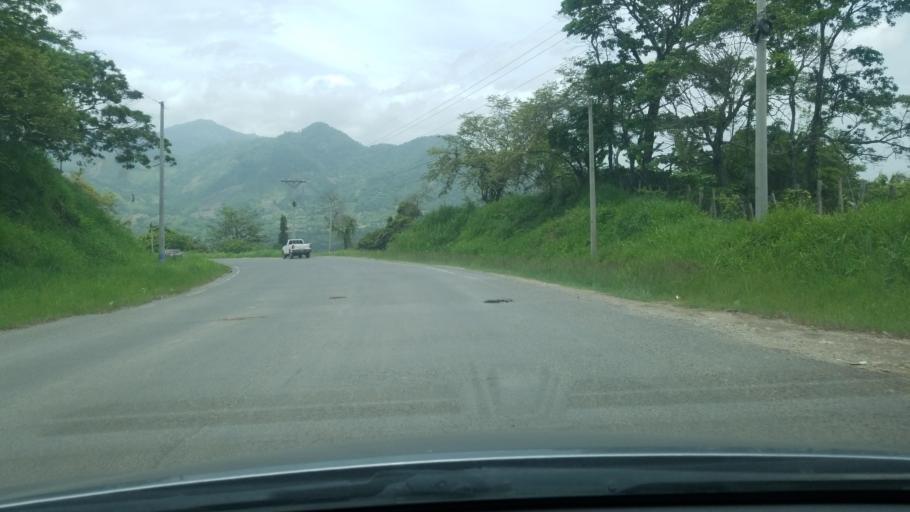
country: HN
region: Copan
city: Santa Rosa de Copan
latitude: 14.7338
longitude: -88.7737
